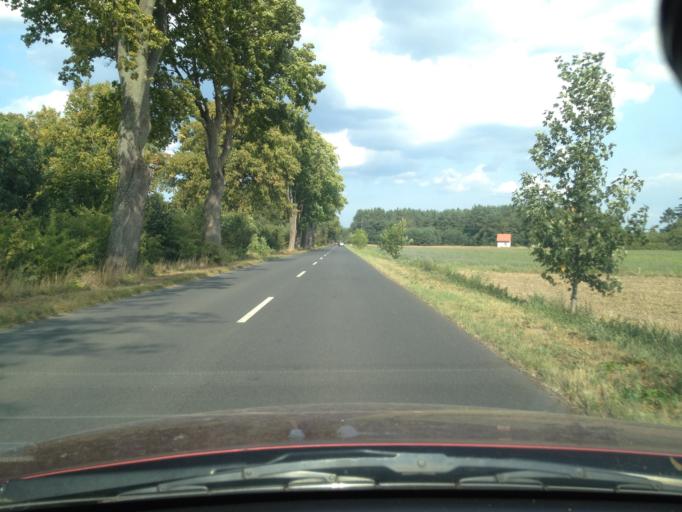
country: PL
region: West Pomeranian Voivodeship
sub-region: Powiat kamienski
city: Dziwnow
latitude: 54.0063
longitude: 14.8425
